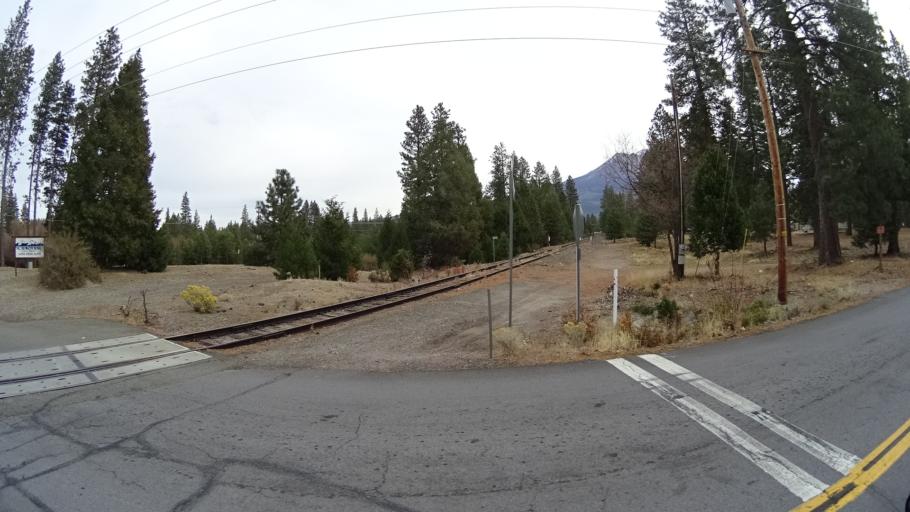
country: US
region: California
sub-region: Siskiyou County
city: Weed
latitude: 41.4009
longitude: -122.3799
